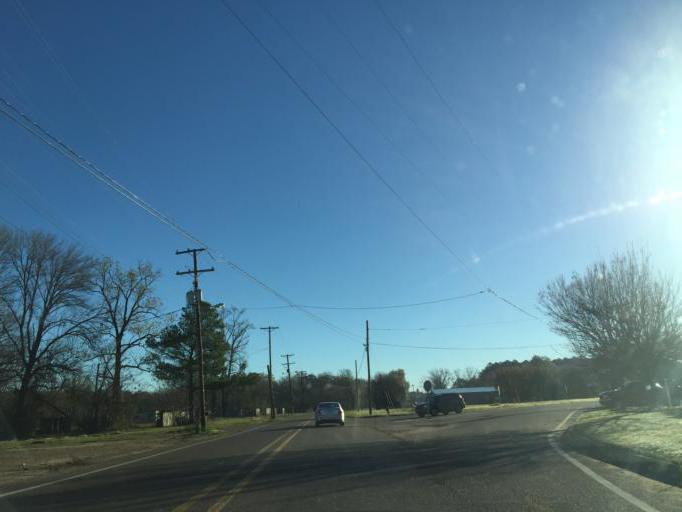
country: US
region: Mississippi
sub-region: Hinds County
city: Jackson
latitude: 32.2830
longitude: -90.1679
